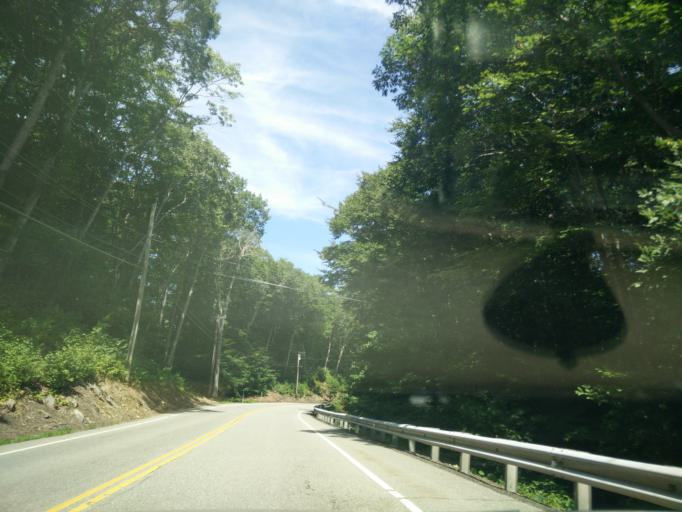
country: US
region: Connecticut
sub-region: Middlesex County
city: Clinton
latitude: 41.3353
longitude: -72.5535
